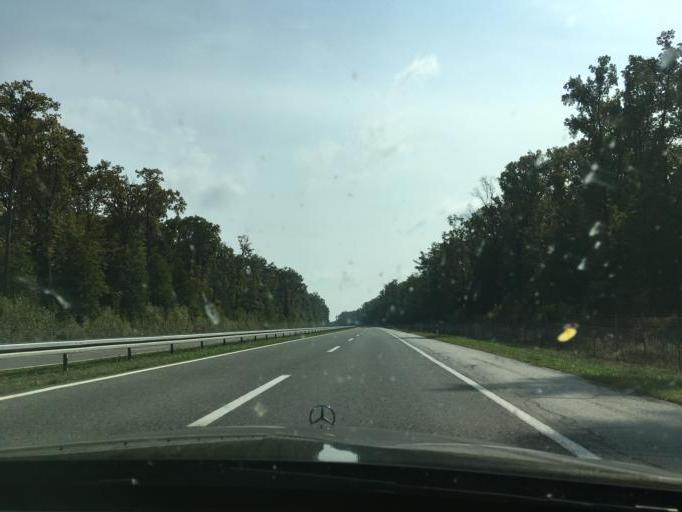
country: HR
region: Vukovarsko-Srijemska
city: Bosnjaci
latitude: 45.0550
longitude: 18.8178
